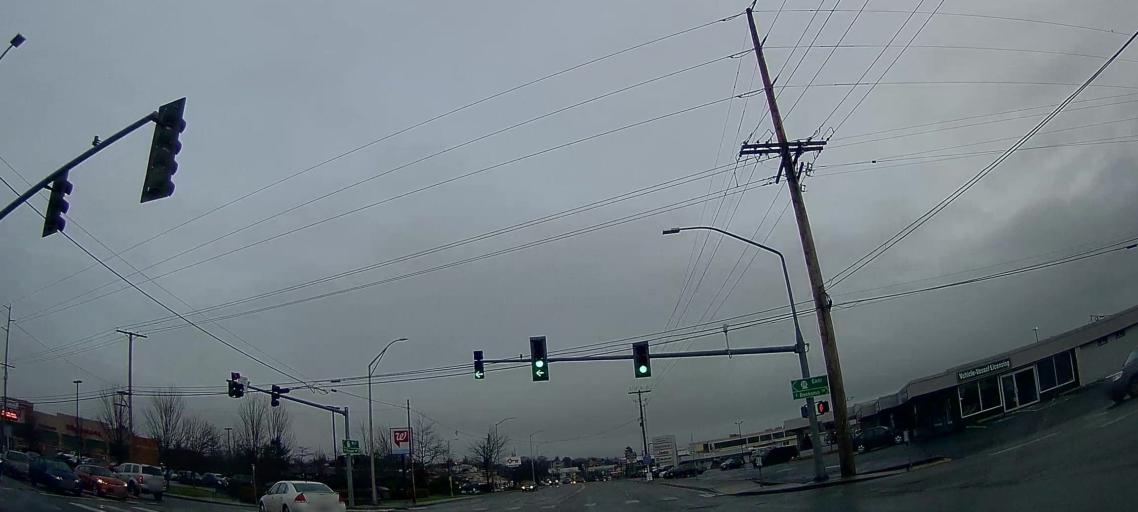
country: US
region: Washington
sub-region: Island County
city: Oak Harbor
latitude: 48.2868
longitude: -122.6579
